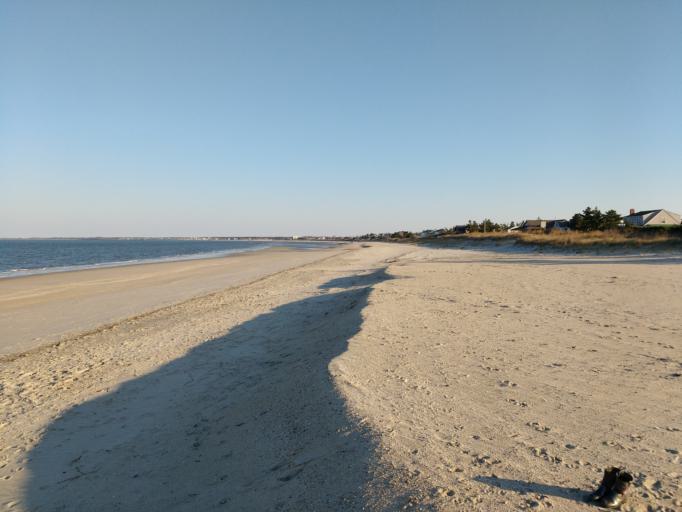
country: US
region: Delaware
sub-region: Sussex County
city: Lewes
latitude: 38.7885
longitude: -75.1550
